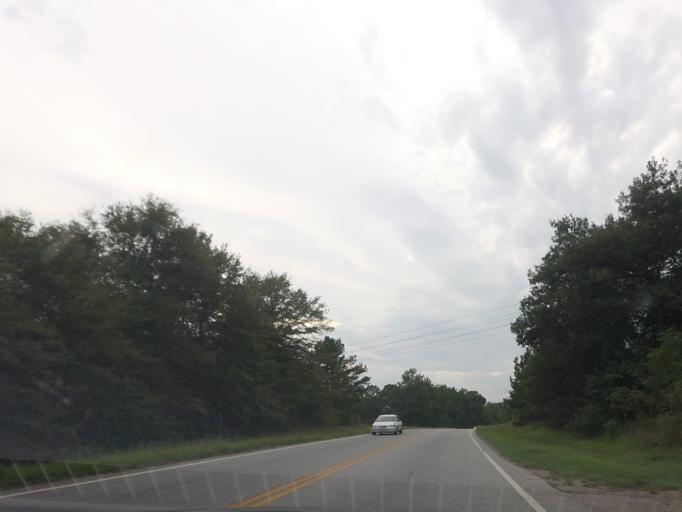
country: US
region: Georgia
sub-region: Twiggs County
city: Jeffersonville
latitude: 32.7617
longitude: -83.4572
